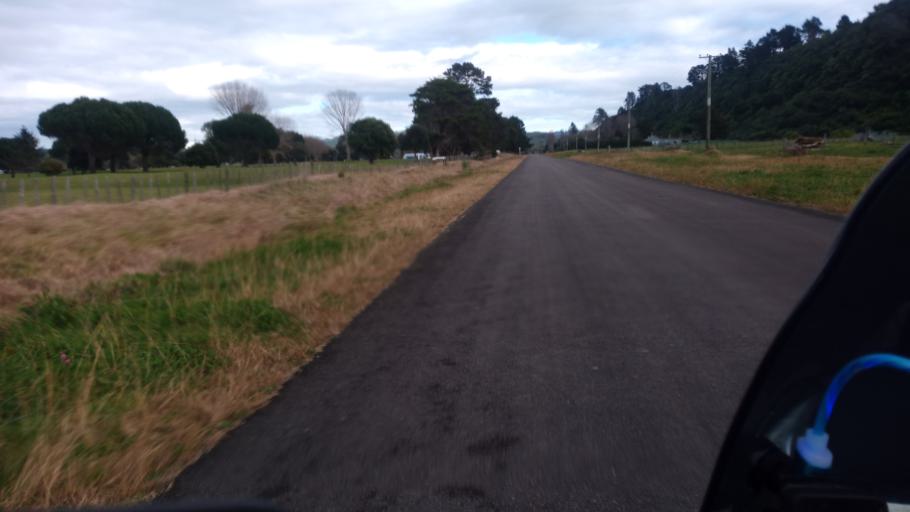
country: NZ
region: Gisborne
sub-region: Gisborne District
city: Gisborne
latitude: -38.3668
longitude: 178.3035
